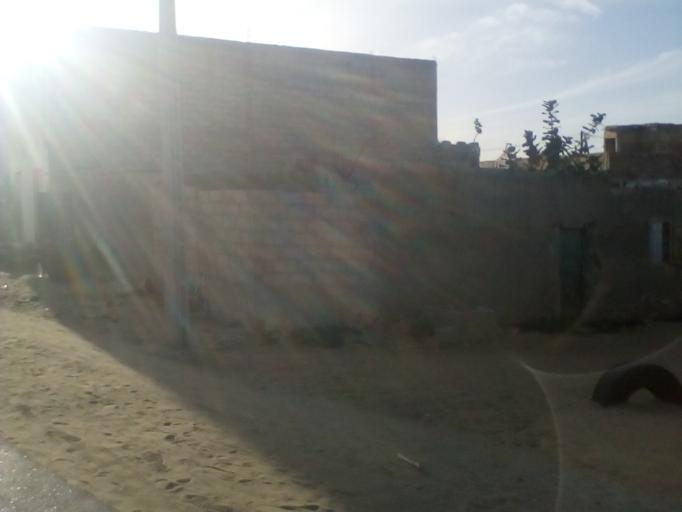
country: SN
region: Saint-Louis
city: Saint-Louis
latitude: 15.9912
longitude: -16.4841
